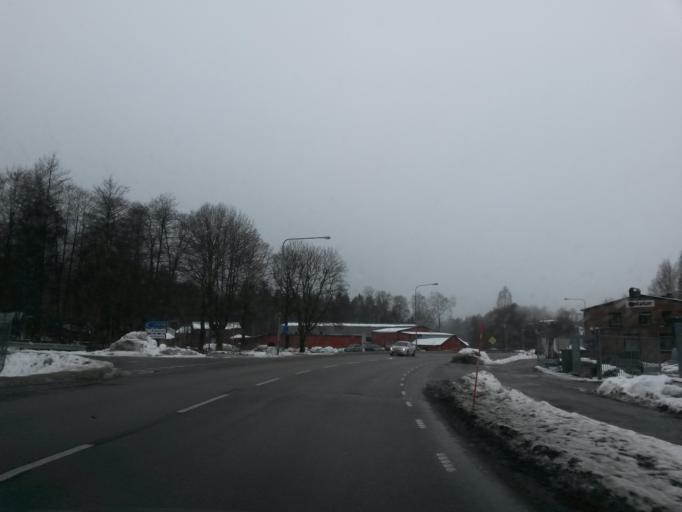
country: SE
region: Vaestra Goetaland
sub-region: Boras Kommun
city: Ganghester
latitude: 57.6965
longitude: 13.0298
